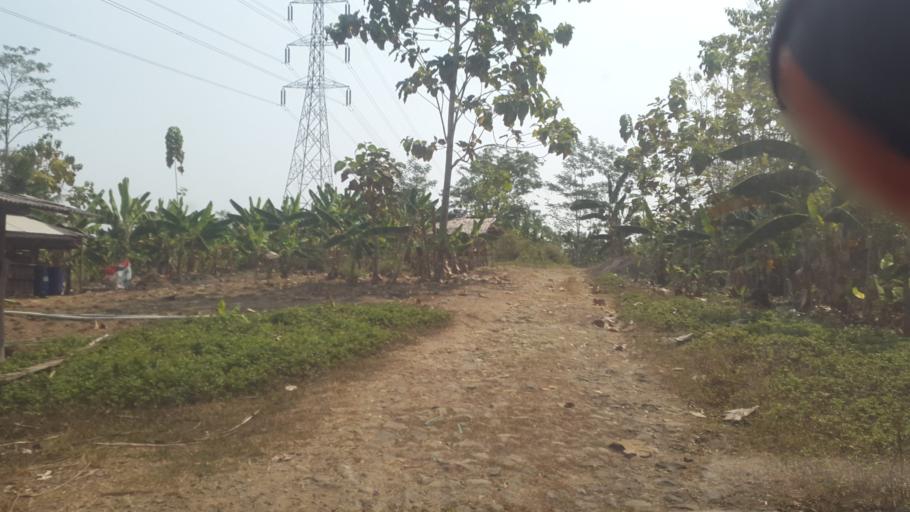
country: ID
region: West Java
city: Cimaja
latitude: -6.9492
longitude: 106.5068
